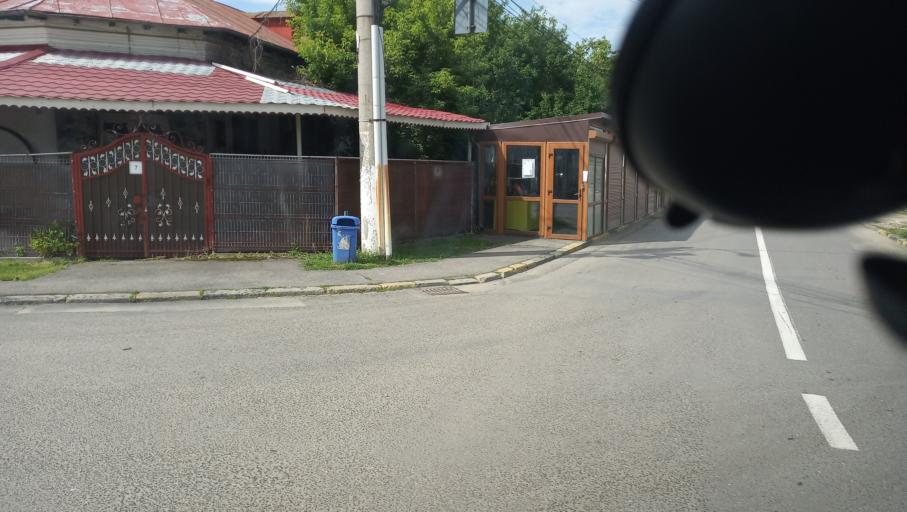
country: RO
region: Ilfov
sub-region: Comuna Otopeni
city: Otopeni
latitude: 44.5341
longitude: 26.0592
